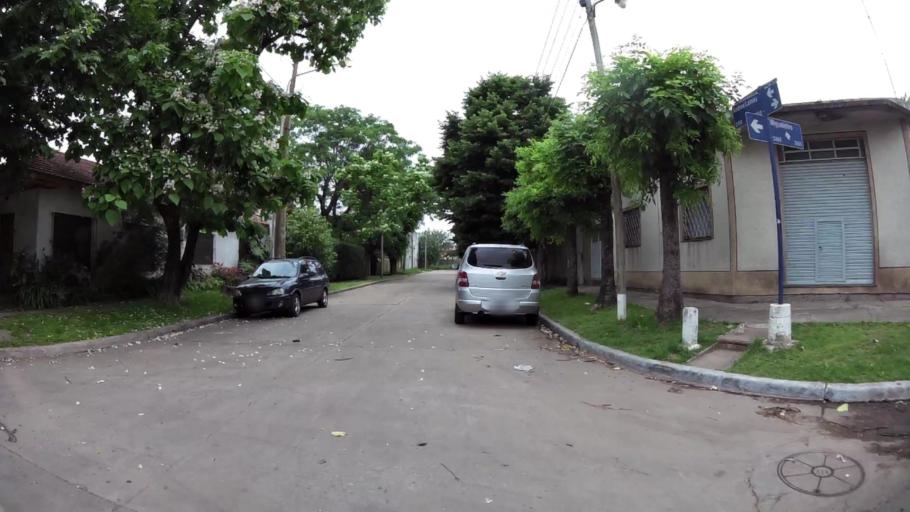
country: AR
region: Buenos Aires
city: San Justo
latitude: -34.7197
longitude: -58.5277
